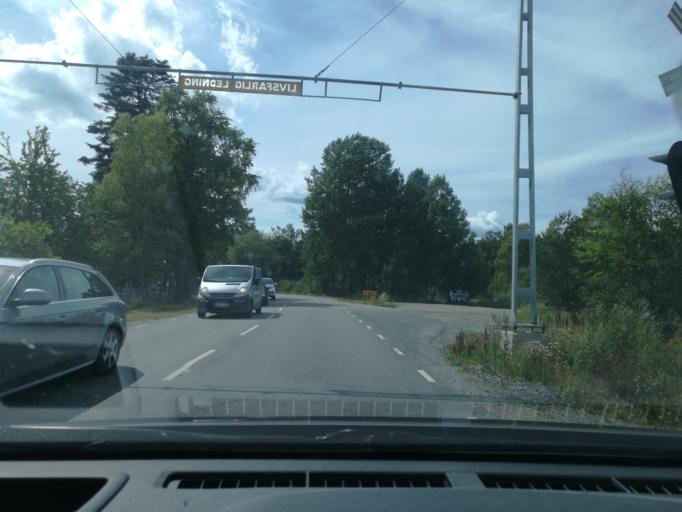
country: SE
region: Stockholm
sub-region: Sigtuna Kommun
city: Rosersberg
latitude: 59.5864
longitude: 17.8786
